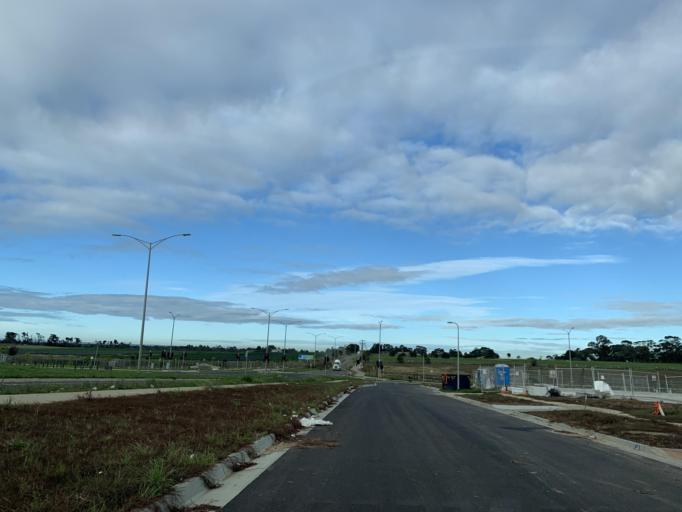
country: AU
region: Victoria
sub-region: Casey
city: Cranbourne East
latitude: -38.1256
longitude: 145.3449
